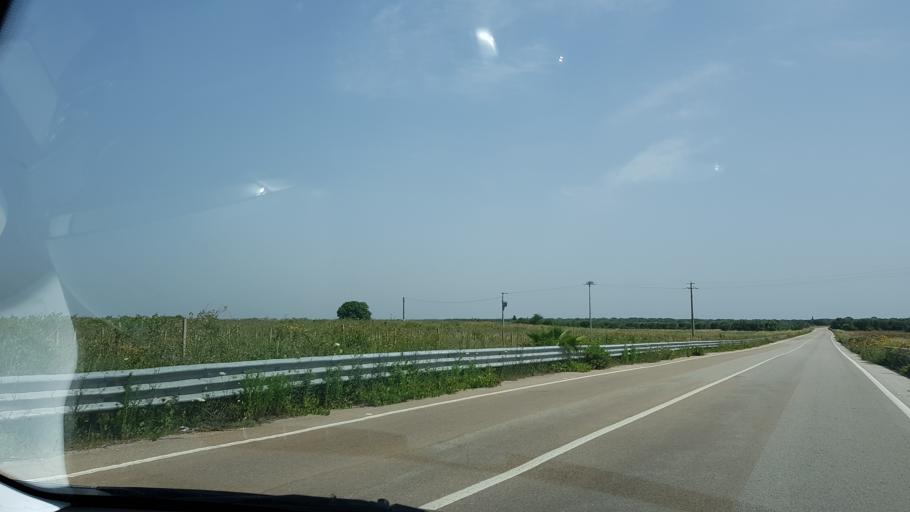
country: IT
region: Apulia
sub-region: Provincia di Brindisi
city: San Pancrazio Salentino
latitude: 40.4804
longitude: 17.8359
